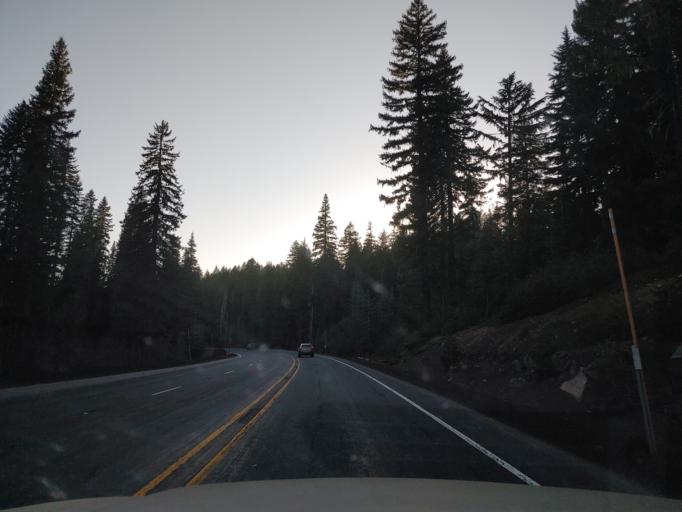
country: US
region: Oregon
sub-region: Lane County
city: Oakridge
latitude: 43.6163
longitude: -122.0990
